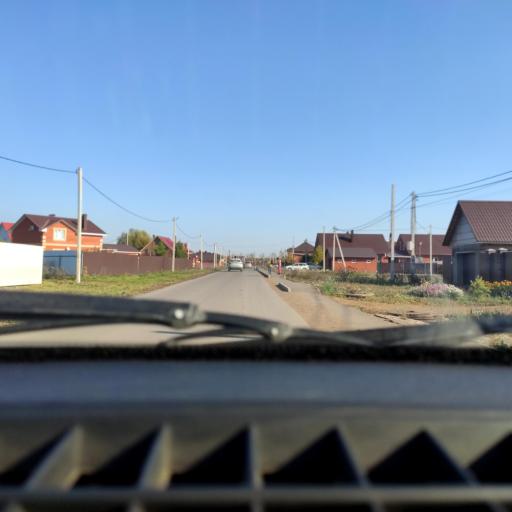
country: RU
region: Bashkortostan
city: Ufa
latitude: 54.6232
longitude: 55.9020
